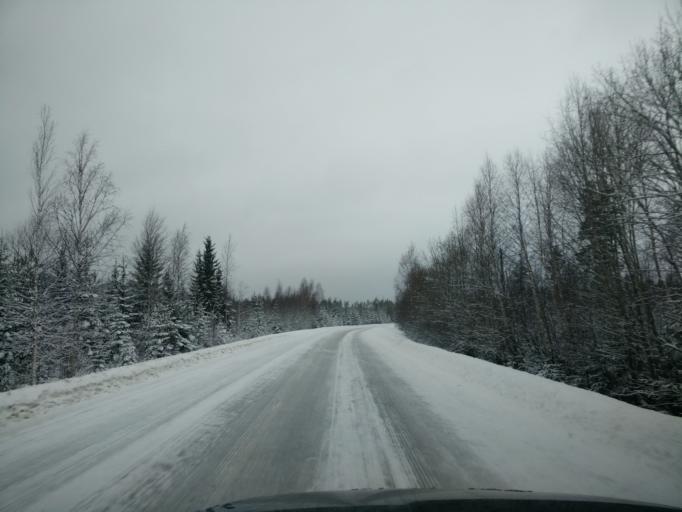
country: SE
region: Vaesternorrland
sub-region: Ange Kommun
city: Ange
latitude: 62.4006
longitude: 15.3245
